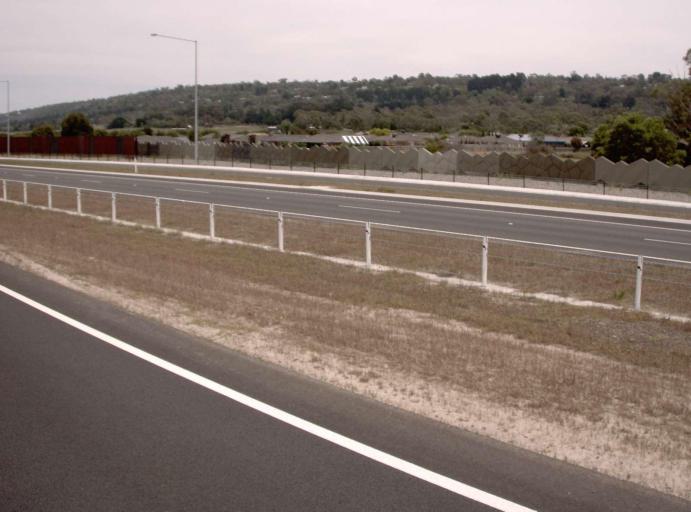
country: AU
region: Victoria
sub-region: Mornington Peninsula
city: Baxter
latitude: -38.1981
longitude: 145.1478
